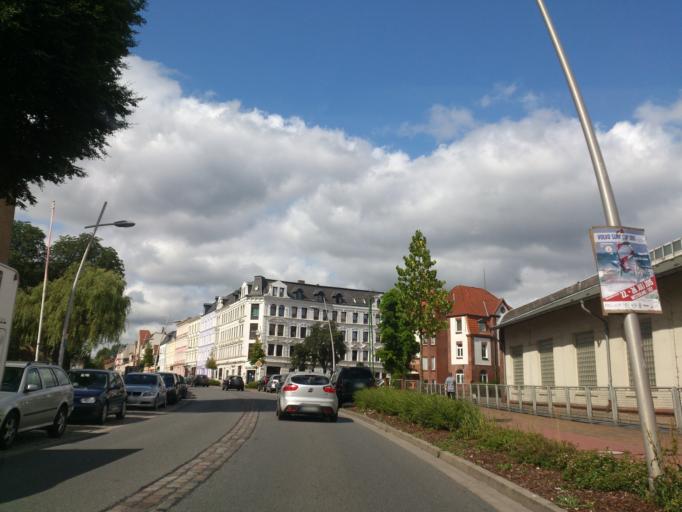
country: DE
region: Schleswig-Holstein
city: Flensburg
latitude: 54.8020
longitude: 9.4244
